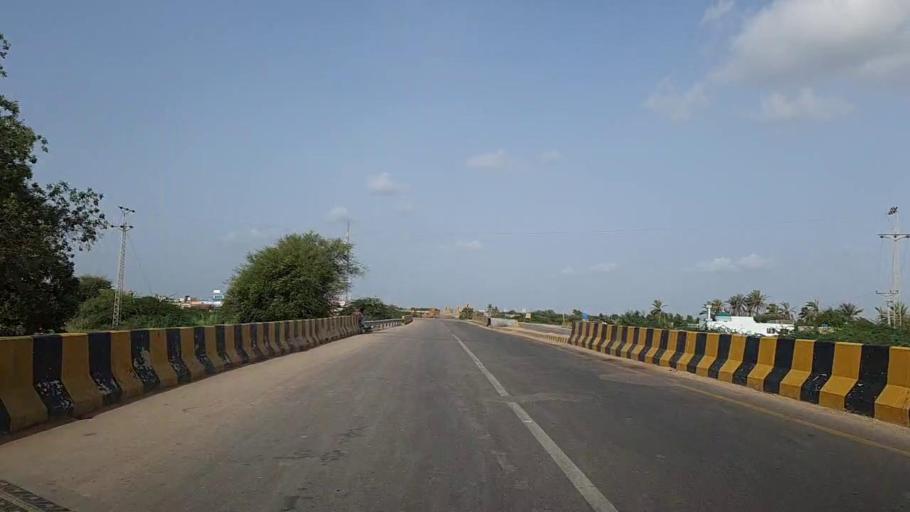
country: PK
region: Sindh
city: Thatta
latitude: 24.7401
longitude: 67.7635
